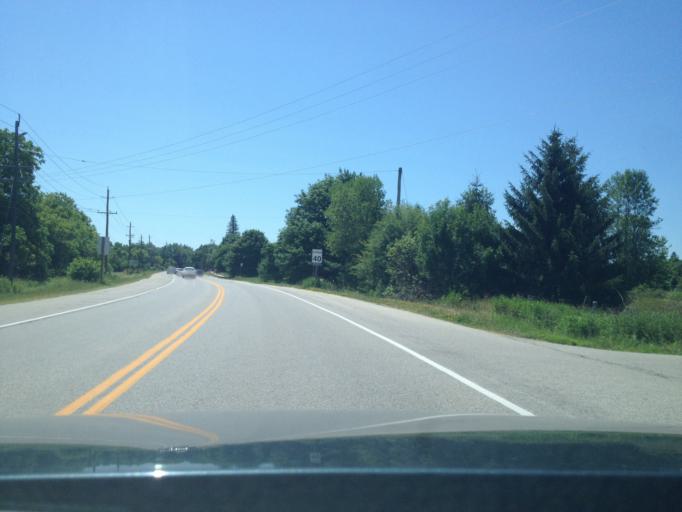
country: CA
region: Ontario
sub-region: Wellington County
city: Guelph
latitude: 43.6896
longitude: -80.4178
